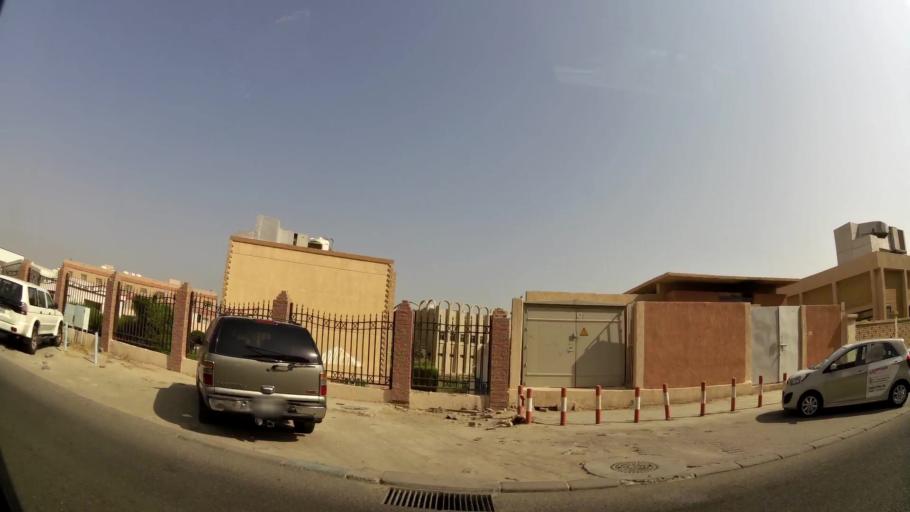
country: KW
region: Muhafazat Hawalli
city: Hawalli
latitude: 29.3429
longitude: 48.0224
